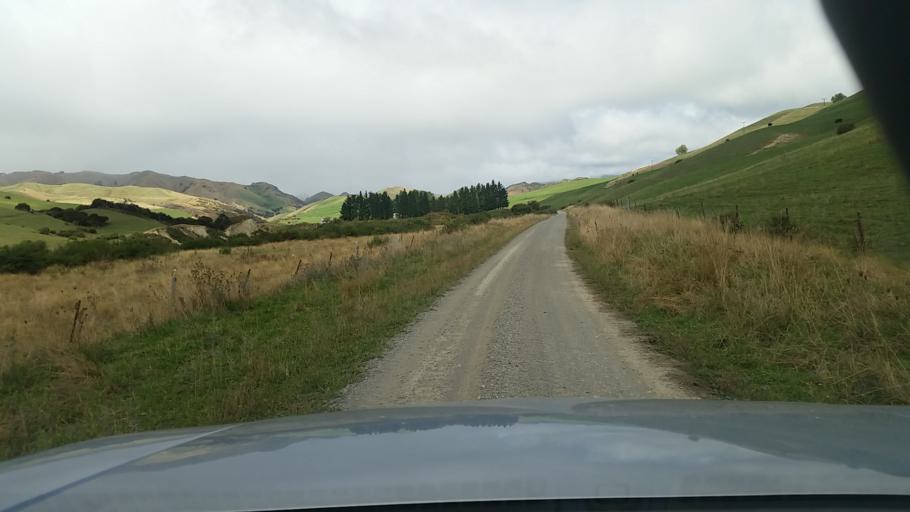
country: NZ
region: Marlborough
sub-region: Marlborough District
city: Blenheim
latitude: -41.7380
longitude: 173.8932
